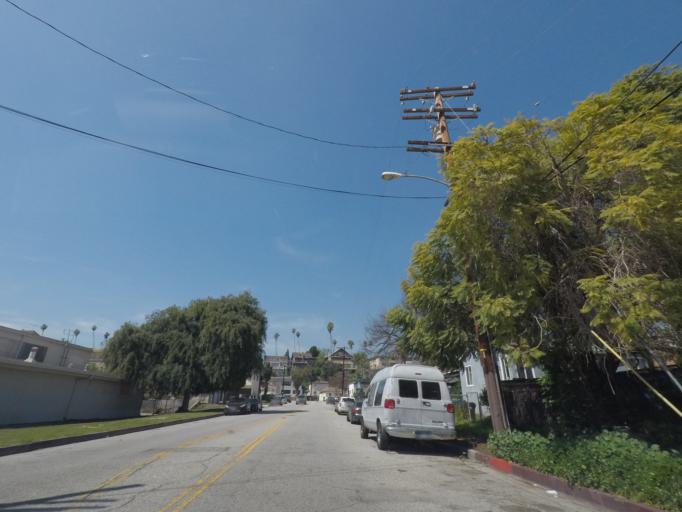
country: US
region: California
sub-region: Los Angeles County
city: South Pasadena
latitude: 34.1136
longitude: -118.1770
